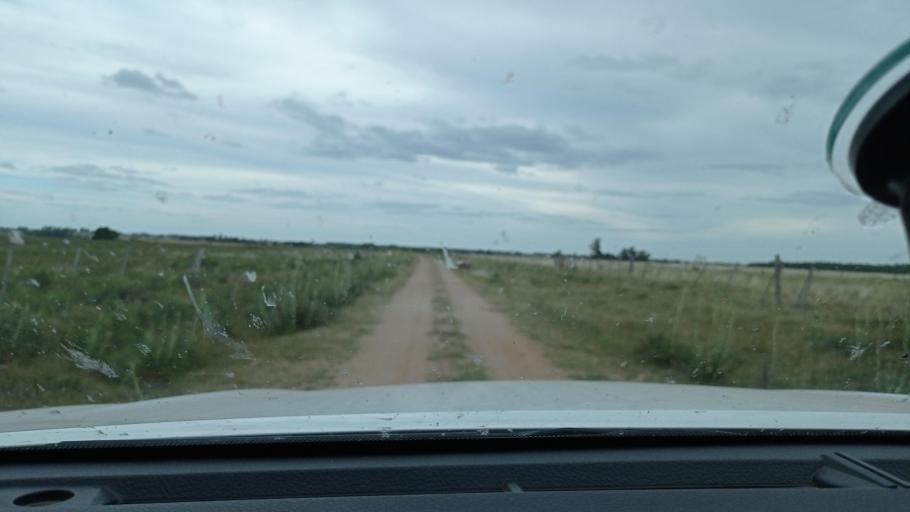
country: UY
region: Florida
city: Casupa
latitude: -34.1290
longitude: -55.8012
